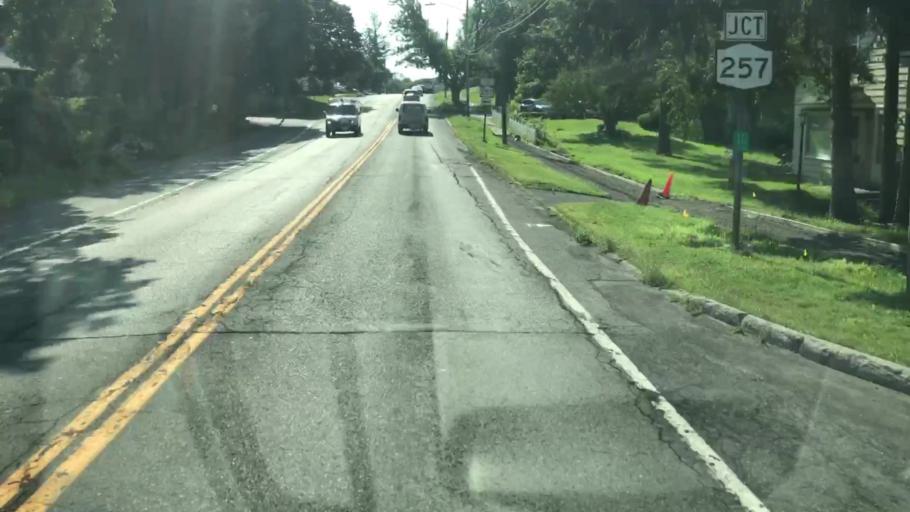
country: US
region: New York
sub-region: Onondaga County
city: Manlius
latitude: 43.0077
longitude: -75.9886
